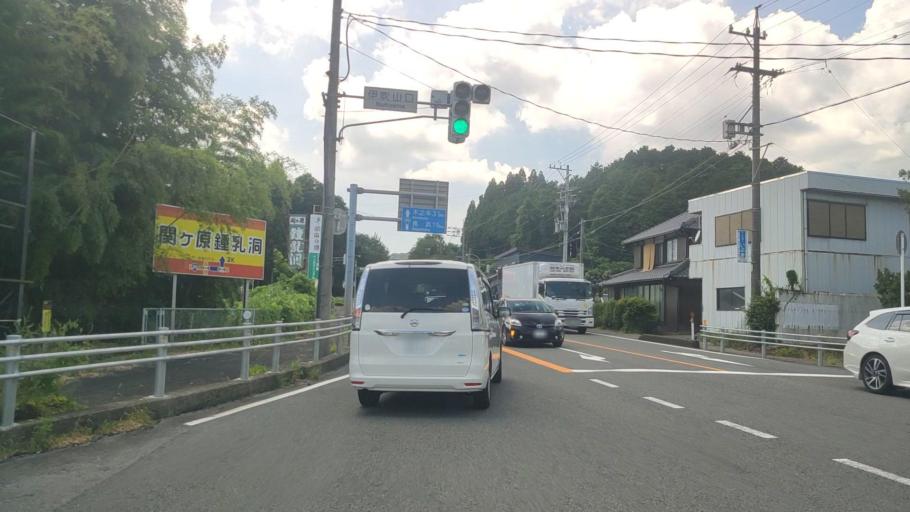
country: JP
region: Gifu
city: Tarui
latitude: 35.3712
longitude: 136.4490
